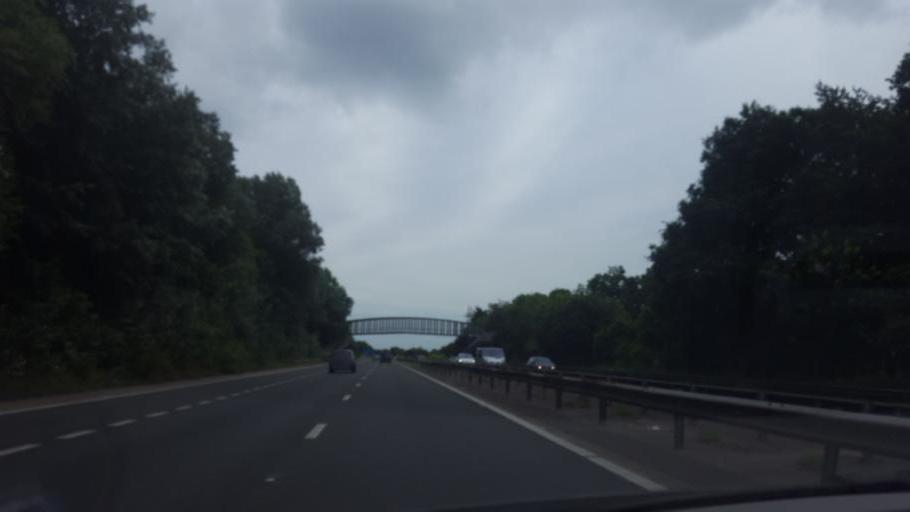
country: GB
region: England
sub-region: Royal Borough of Windsor and Maidenhead
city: Maidenhead
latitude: 51.5058
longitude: -0.7324
